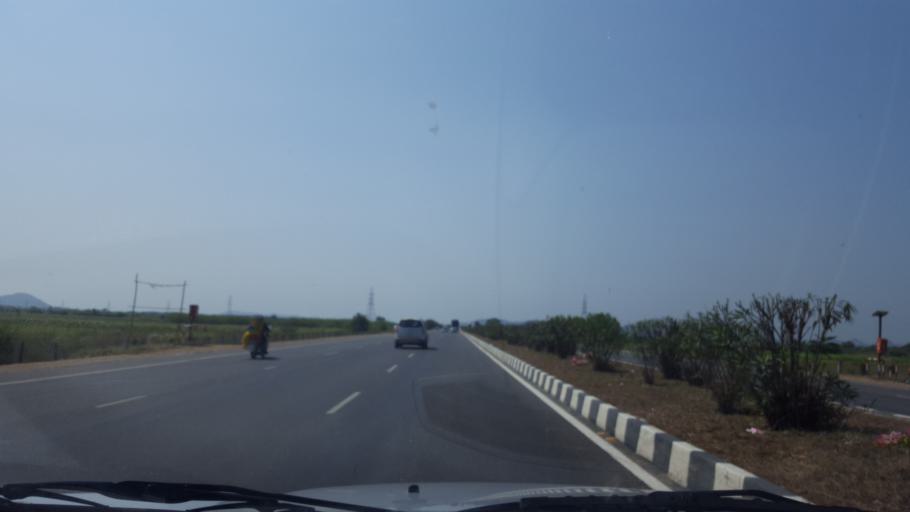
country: IN
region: Andhra Pradesh
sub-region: Guntur
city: Chilakalurupet
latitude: 16.0279
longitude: 80.1281
